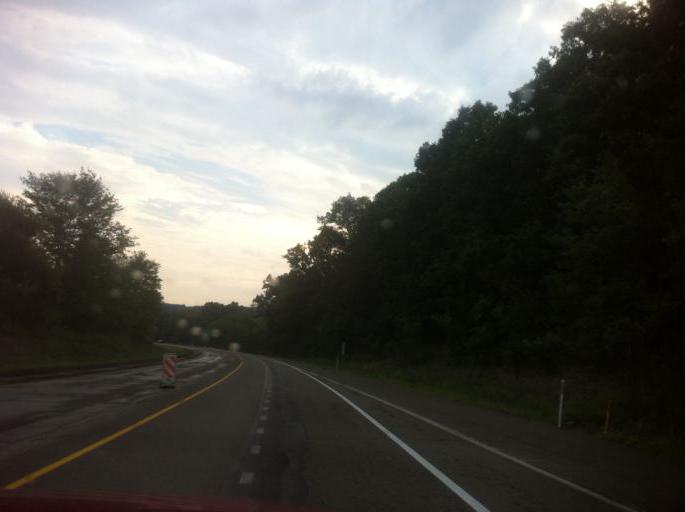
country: US
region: Pennsylvania
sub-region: Clarion County
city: Knox
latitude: 41.1956
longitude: -79.5076
